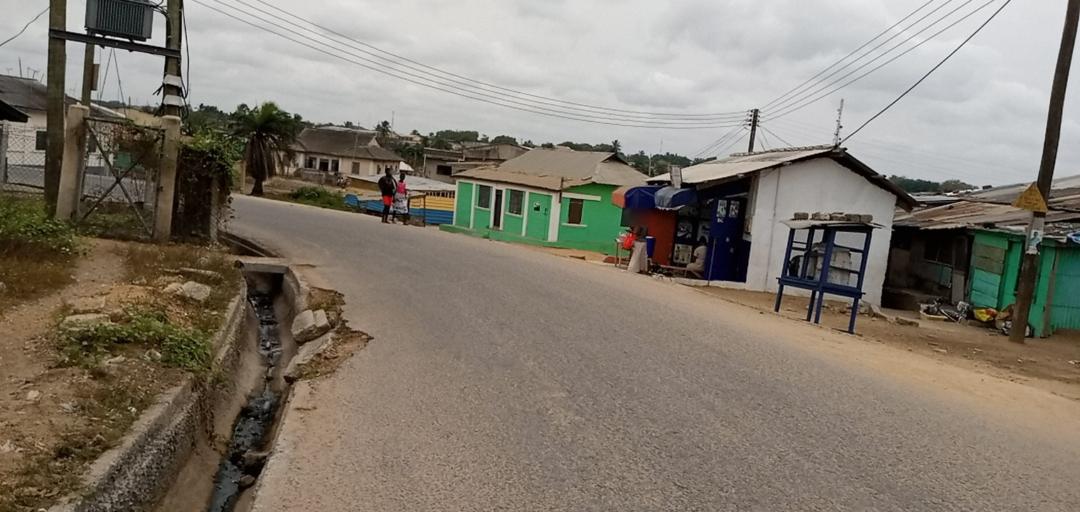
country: GH
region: Central
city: Winneba
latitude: 5.3480
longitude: -0.6209
